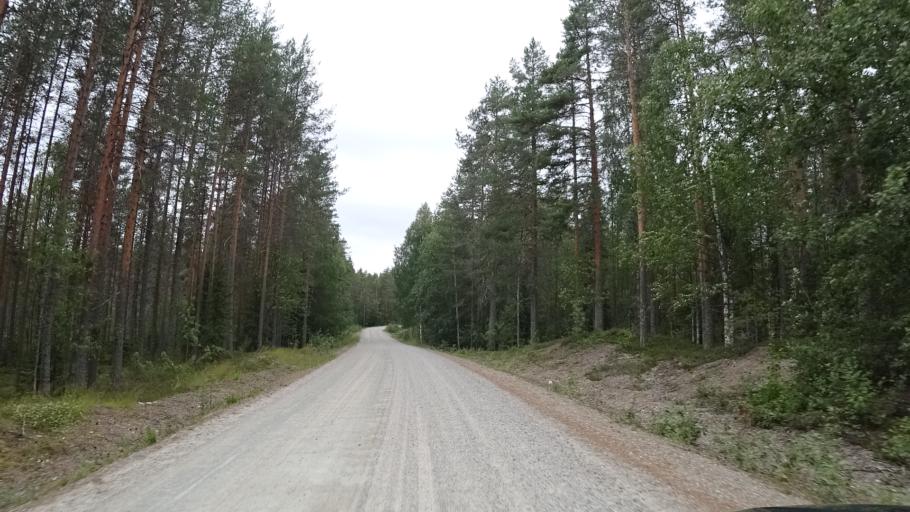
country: FI
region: North Karelia
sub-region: Pielisen Karjala
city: Lieksa
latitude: 63.2083
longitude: 30.4292
